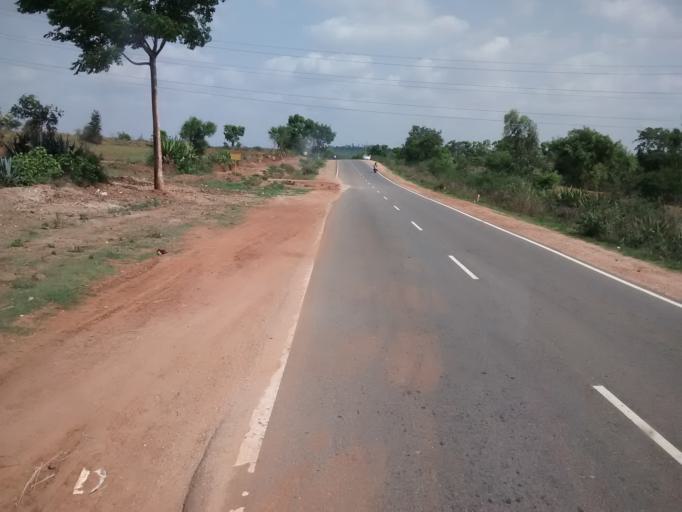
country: IN
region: Karnataka
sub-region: Mysore
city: Hunsur
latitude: 12.3582
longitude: 76.4241
